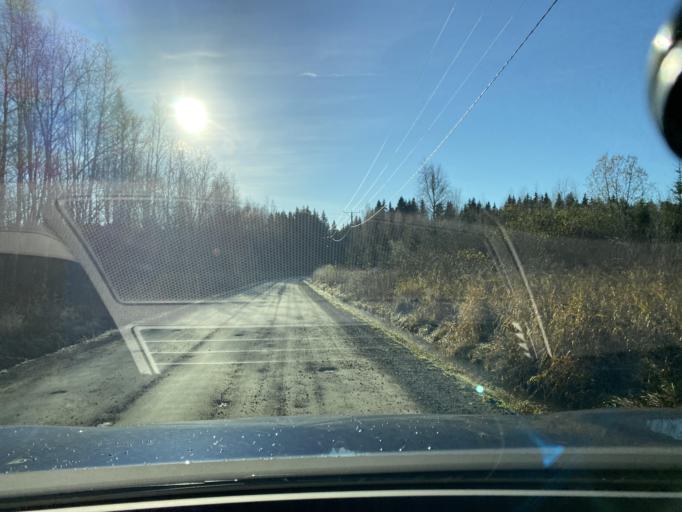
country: FI
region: Pirkanmaa
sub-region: Etelae-Pirkanmaa
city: Akaa
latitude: 61.0113
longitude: 23.9154
